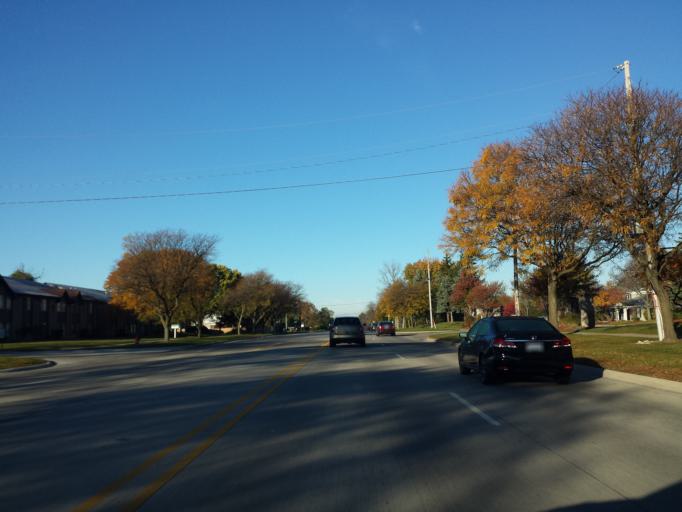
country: US
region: Michigan
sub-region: Oakland County
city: Bingham Farms
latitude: 42.5015
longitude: -83.2630
